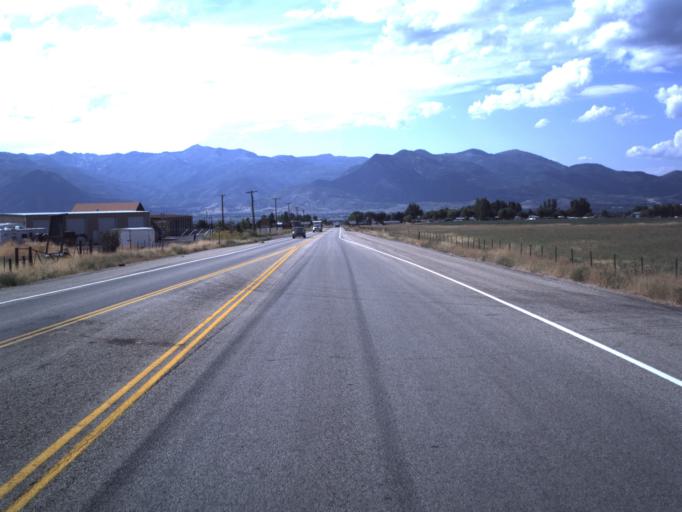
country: US
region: Utah
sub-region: Wasatch County
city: Heber
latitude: 40.4644
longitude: -111.3842
